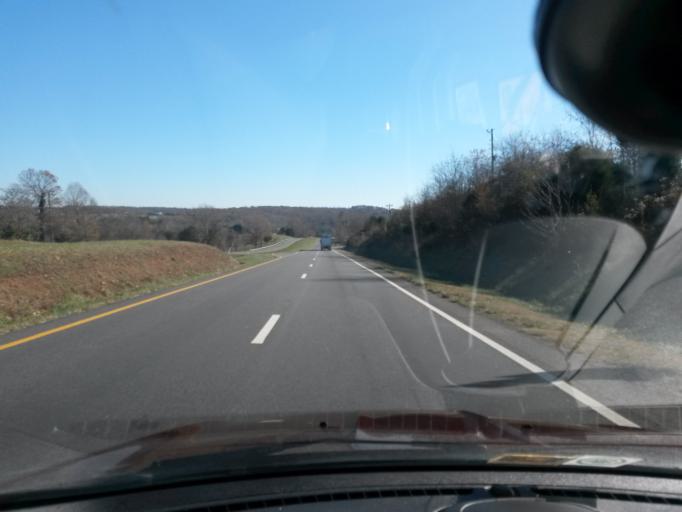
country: US
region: Virginia
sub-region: City of Bedford
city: Bedford
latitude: 37.3119
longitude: -79.4024
